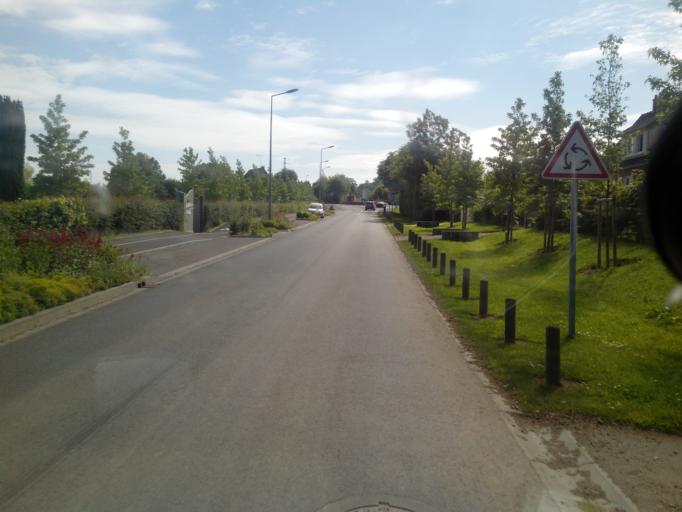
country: FR
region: Lower Normandy
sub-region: Departement du Calvados
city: Saint-Gatien-des-Bois
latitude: 49.2798
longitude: 0.1766
